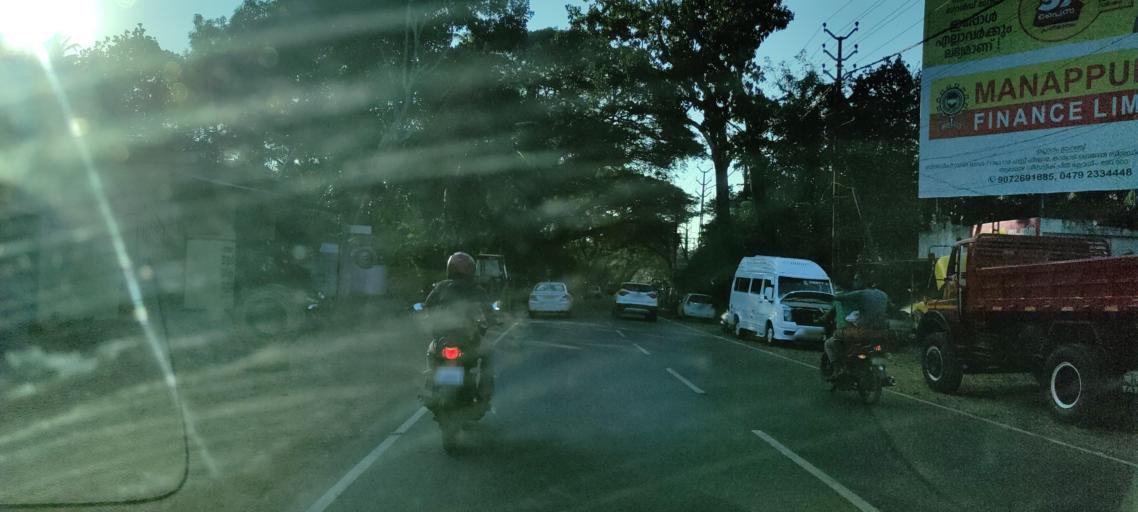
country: IN
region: Kerala
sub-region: Alappuzha
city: Kattanam
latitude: 9.1761
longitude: 76.5714
